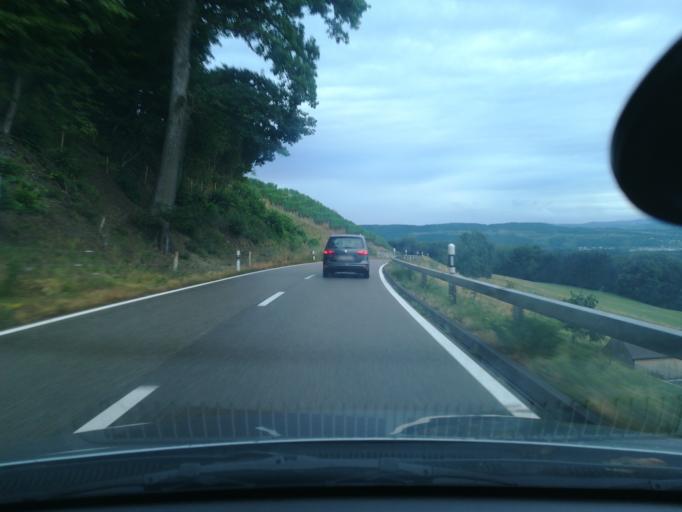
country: CH
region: Thurgau
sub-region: Frauenfeld District
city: Huttwilen
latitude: 47.6101
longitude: 8.8913
